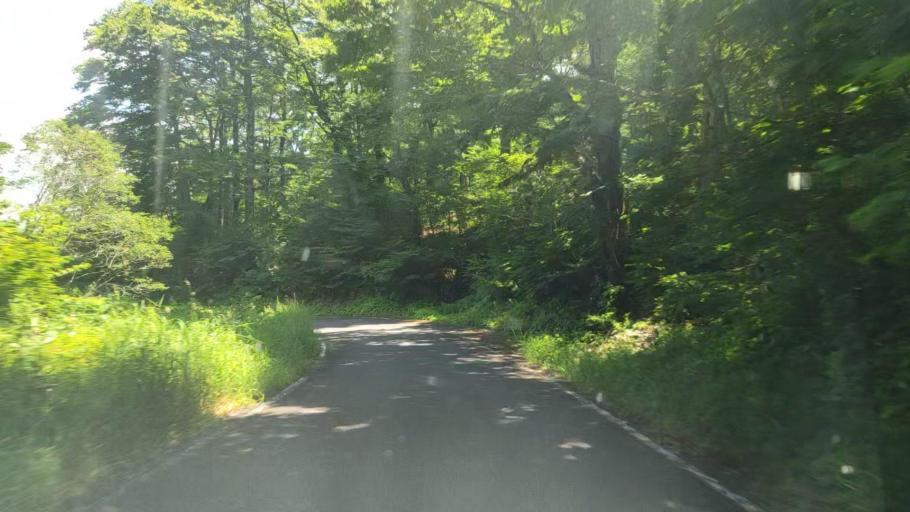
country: JP
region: Fukui
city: Ono
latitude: 35.7732
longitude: 136.5291
